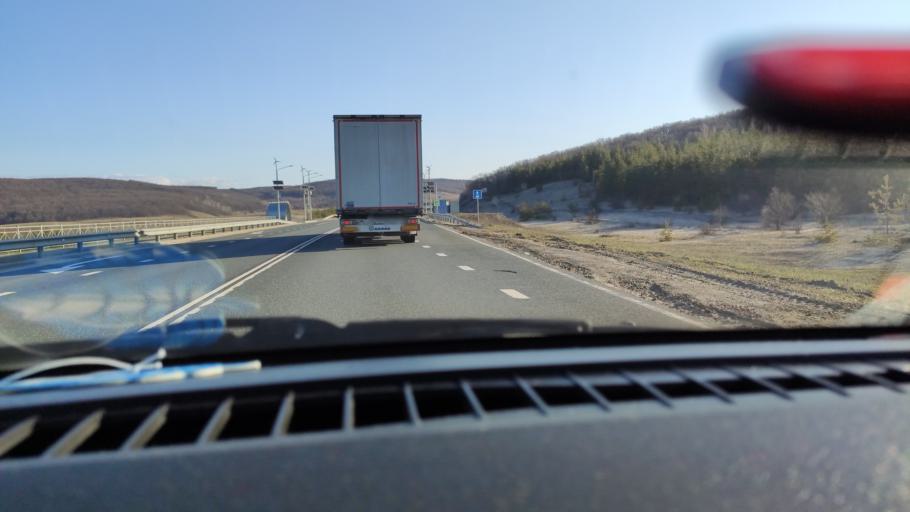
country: RU
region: Saratov
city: Alekseyevka
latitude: 52.3907
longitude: 47.9768
